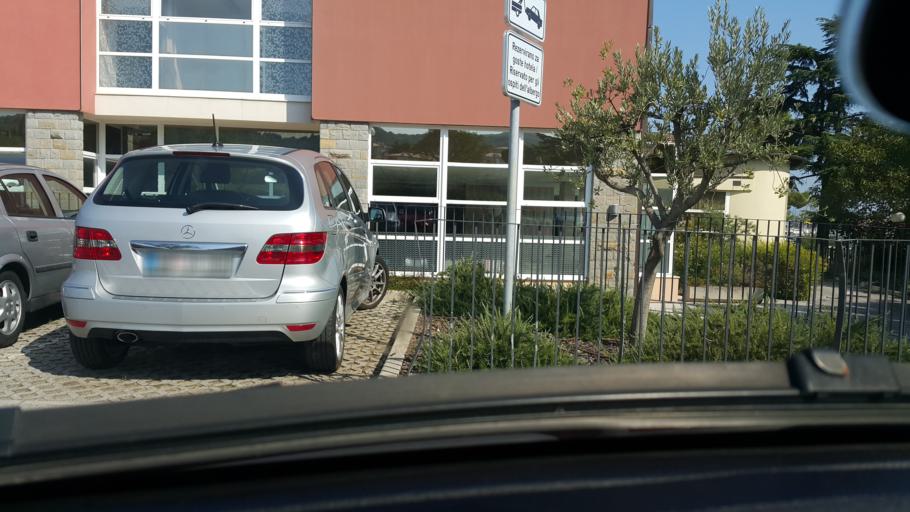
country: SI
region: Izola-Isola
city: Jagodje
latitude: 45.5324
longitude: 13.6514
